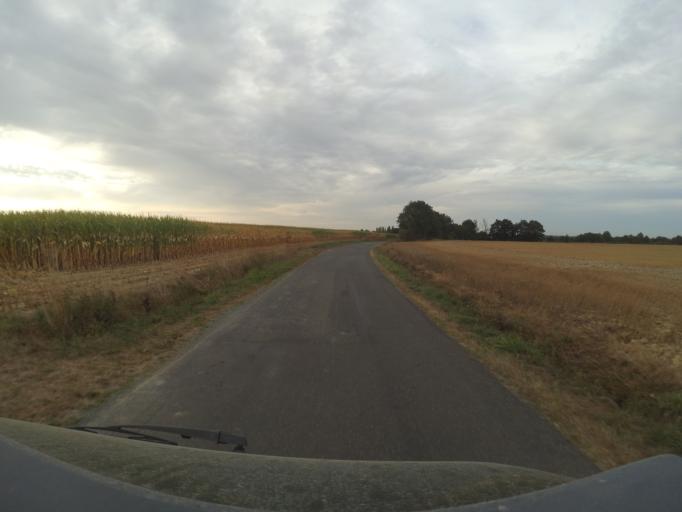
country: FR
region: Pays de la Loire
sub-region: Departement de la Loire-Atlantique
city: Vieillevigne
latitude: 46.9930
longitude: -1.4602
